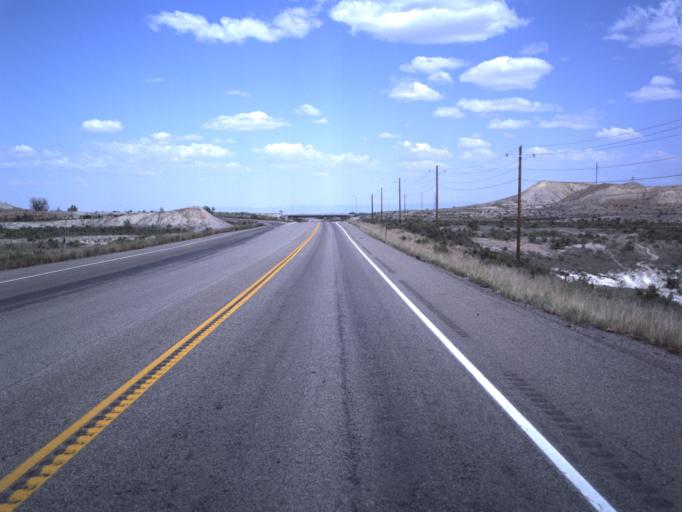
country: US
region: Utah
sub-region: Emery County
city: Castle Dale
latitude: 39.1715
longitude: -111.0542
